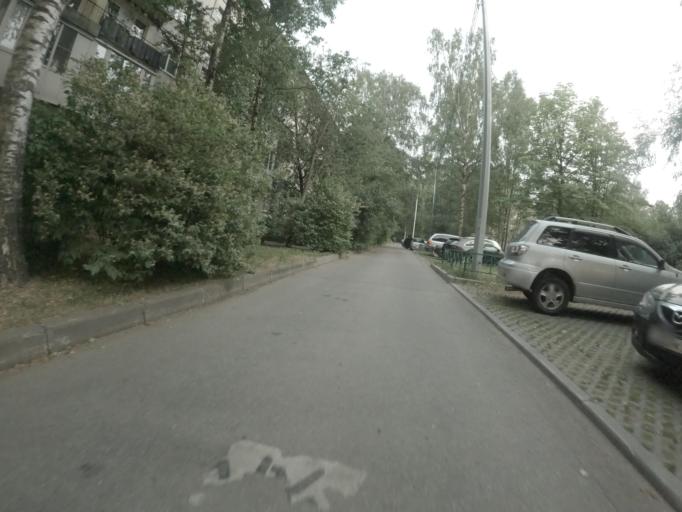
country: RU
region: St.-Petersburg
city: Krasnogvargeisky
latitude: 59.9562
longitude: 30.4443
